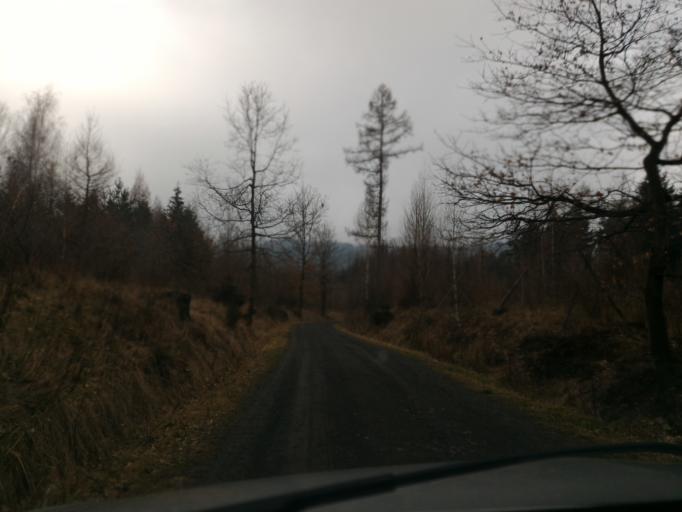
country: DE
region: Saxony
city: Olbersdorf
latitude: 50.8579
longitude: 14.7729
